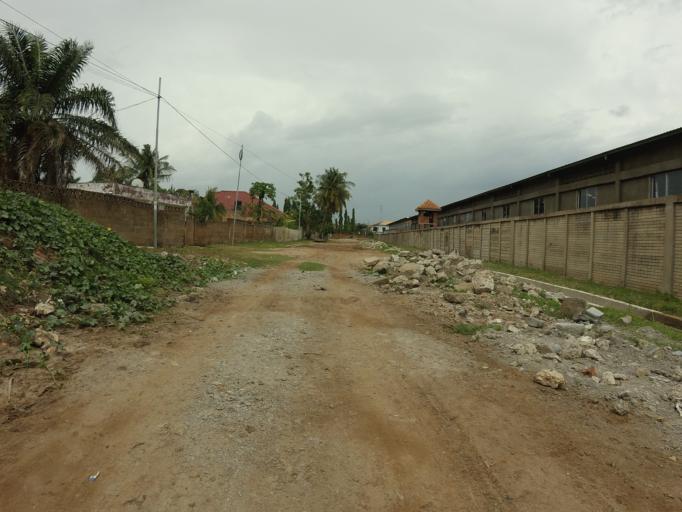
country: GH
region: Greater Accra
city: Accra
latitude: 5.6031
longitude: -0.2120
